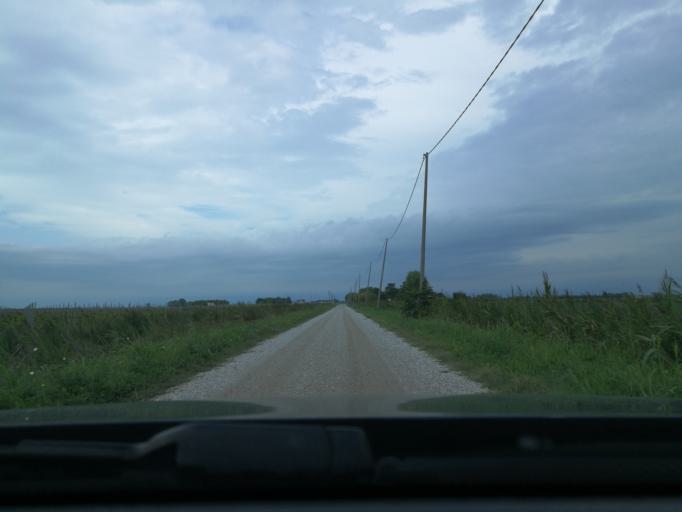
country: IT
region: Friuli Venezia Giulia
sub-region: Provincia di Udine
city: Pertegada
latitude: 45.7193
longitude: 13.0695
